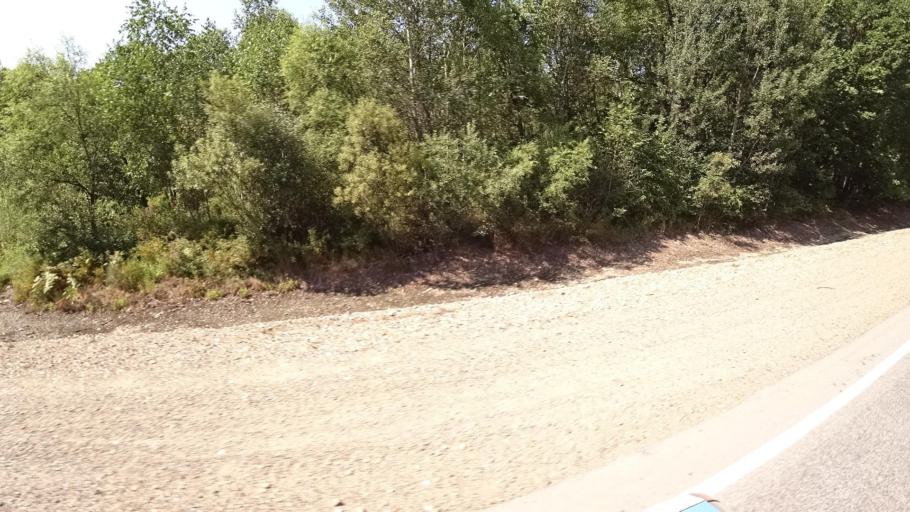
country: RU
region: Khabarovsk Krai
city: Khor
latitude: 47.9842
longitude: 135.0886
